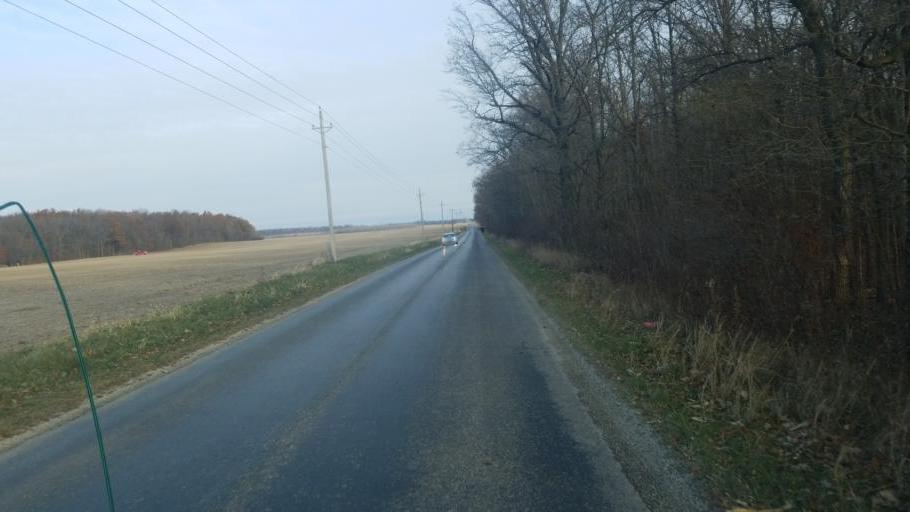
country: US
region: Indiana
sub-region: Adams County
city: Geneva
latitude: 40.5513
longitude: -84.9917
